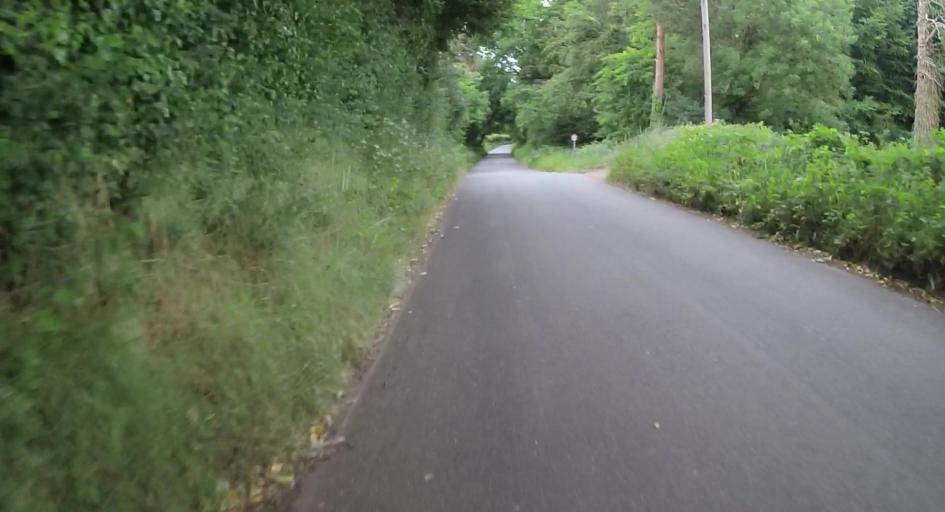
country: GB
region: England
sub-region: Surrey
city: Seale
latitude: 51.2141
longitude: -0.7360
